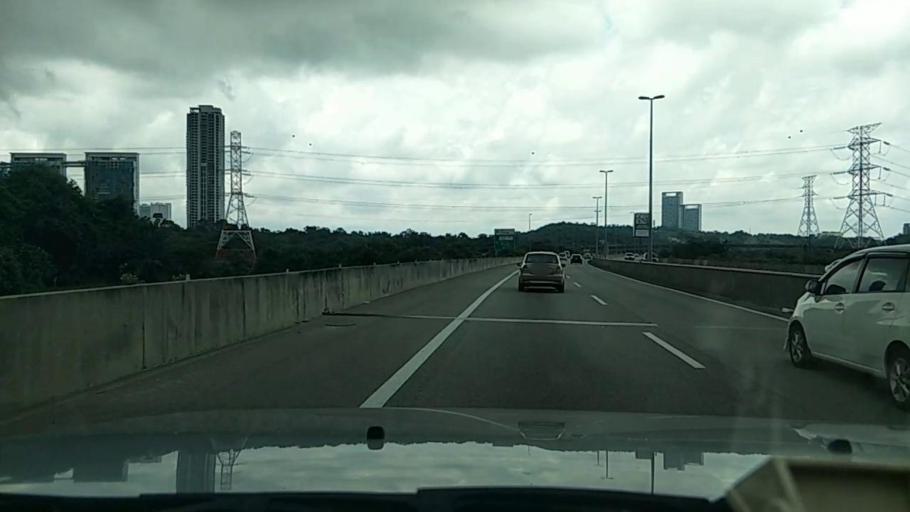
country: MY
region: Putrajaya
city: Putrajaya
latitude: 2.9465
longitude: 101.6464
